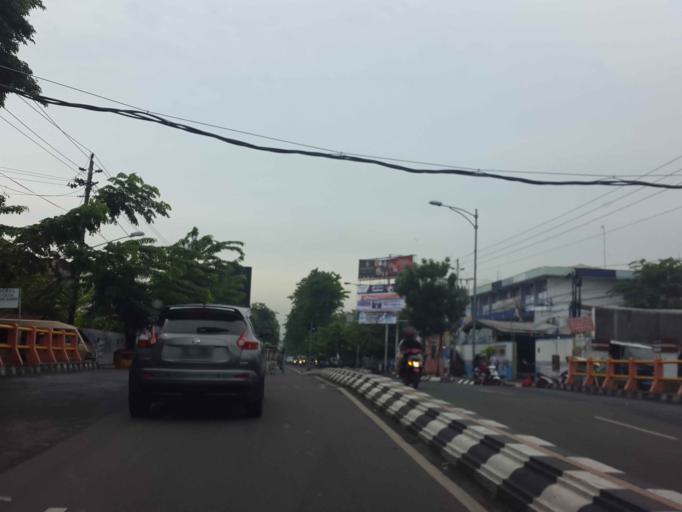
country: ID
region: Central Java
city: Semarang
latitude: -6.9803
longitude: 110.4212
